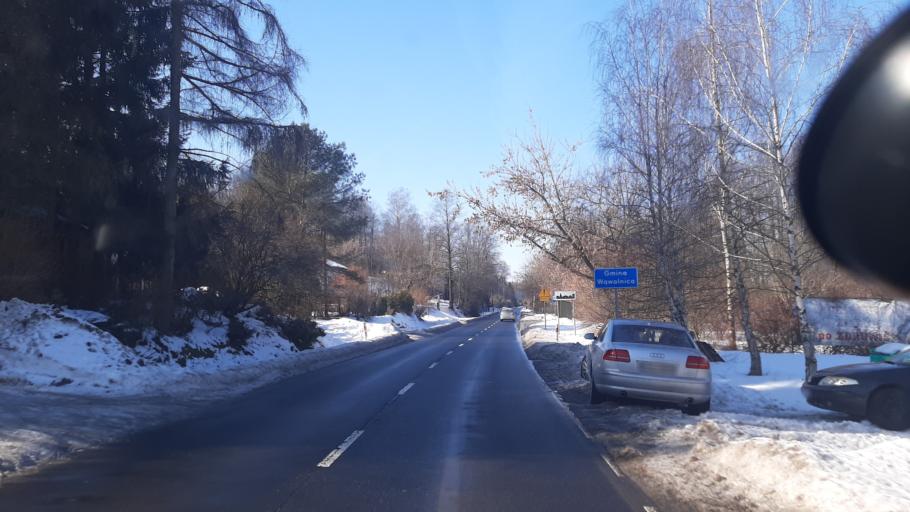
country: PL
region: Lublin Voivodeship
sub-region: Powiat pulawski
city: Naleczow
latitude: 51.2834
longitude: 22.1849
